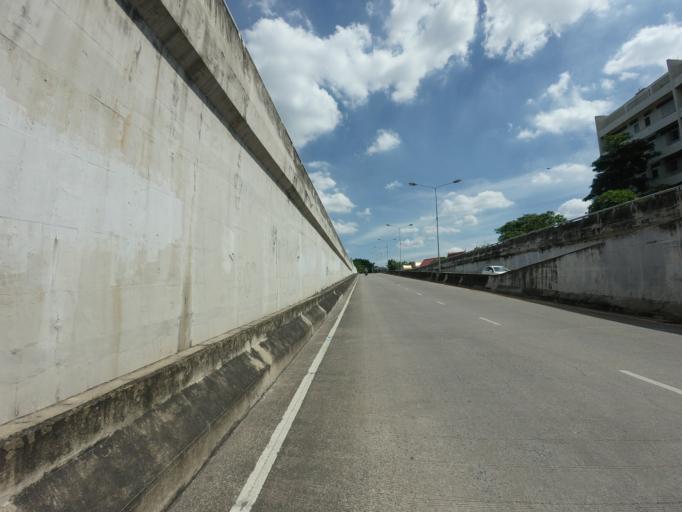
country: TH
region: Bangkok
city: Lak Si
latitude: 13.8549
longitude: 100.5893
